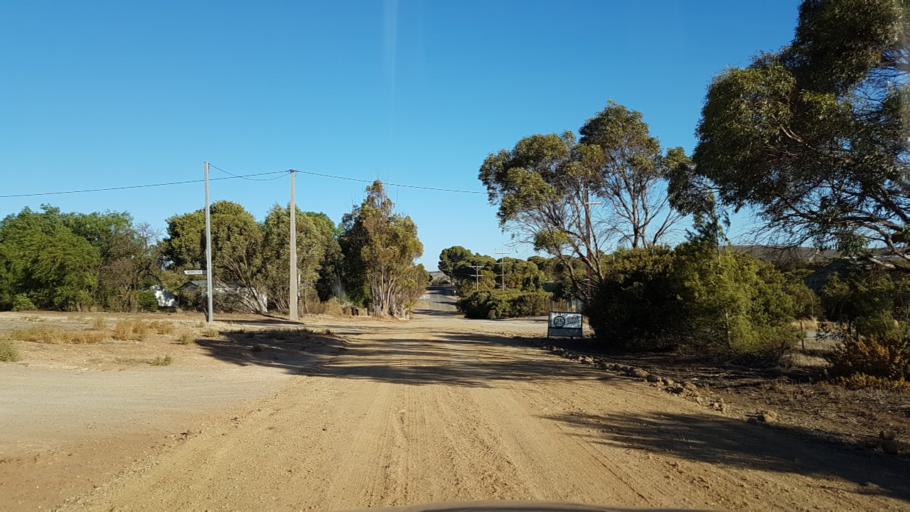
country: AU
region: South Australia
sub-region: Clare and Gilbert Valleys
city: Clare
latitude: -33.6679
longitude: 138.9333
